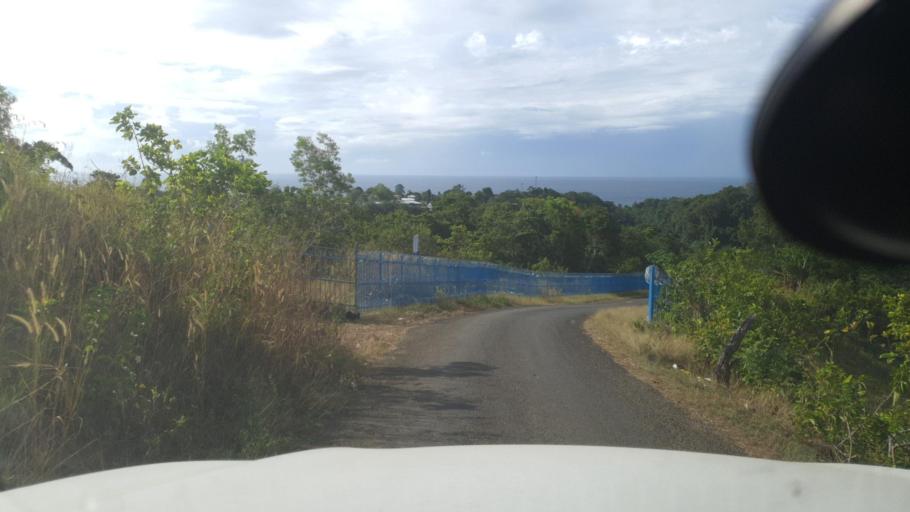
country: SB
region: Guadalcanal
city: Honiara
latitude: -9.4417
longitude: 159.9378
